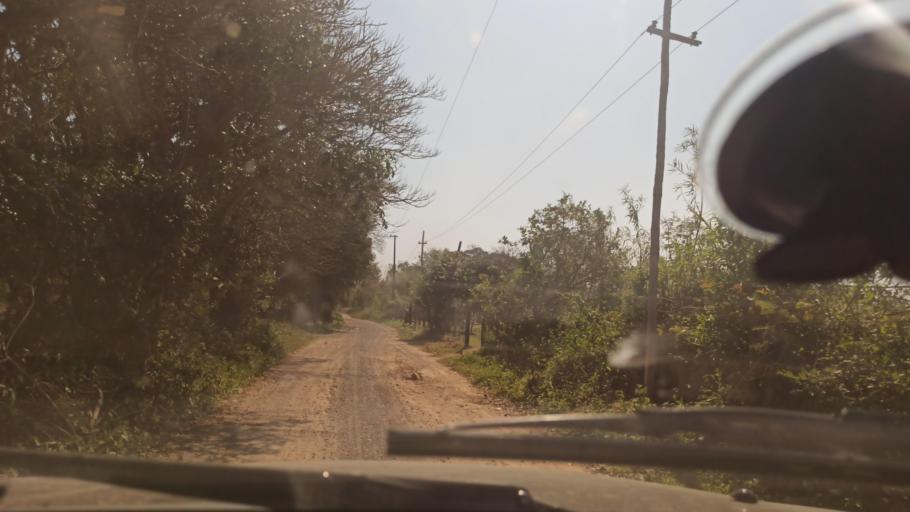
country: AR
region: Formosa
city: Clorinda
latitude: -25.3286
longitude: -57.6913
